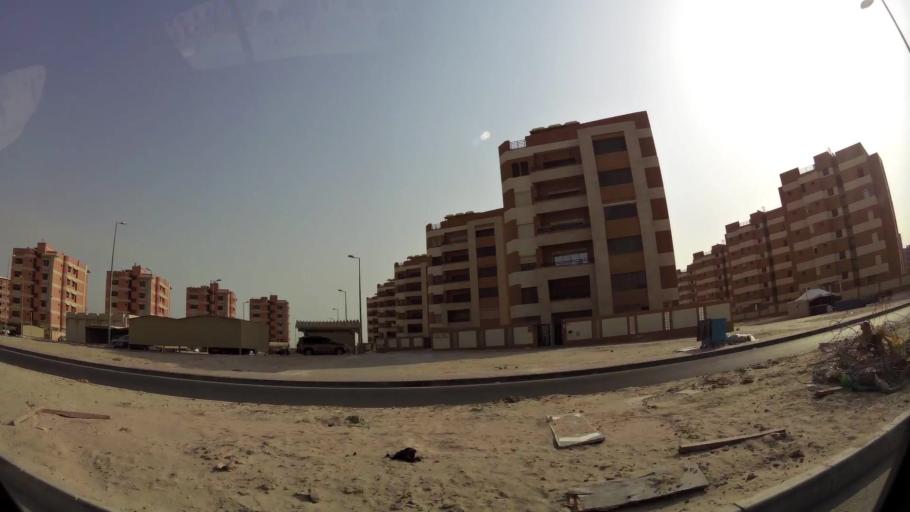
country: KW
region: Al Asimah
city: Ar Rabiyah
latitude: 29.3321
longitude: 47.8129
